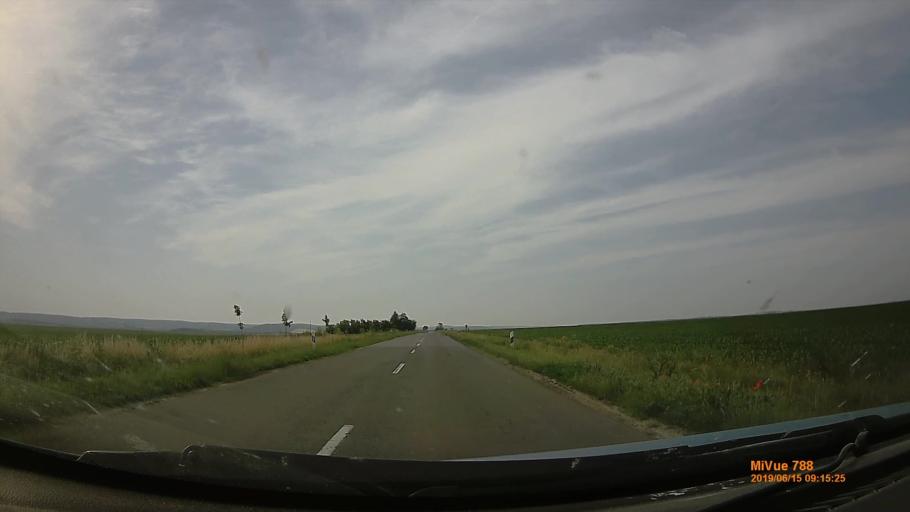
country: HU
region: Tolna
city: Iregszemcse
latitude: 46.6303
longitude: 18.2004
